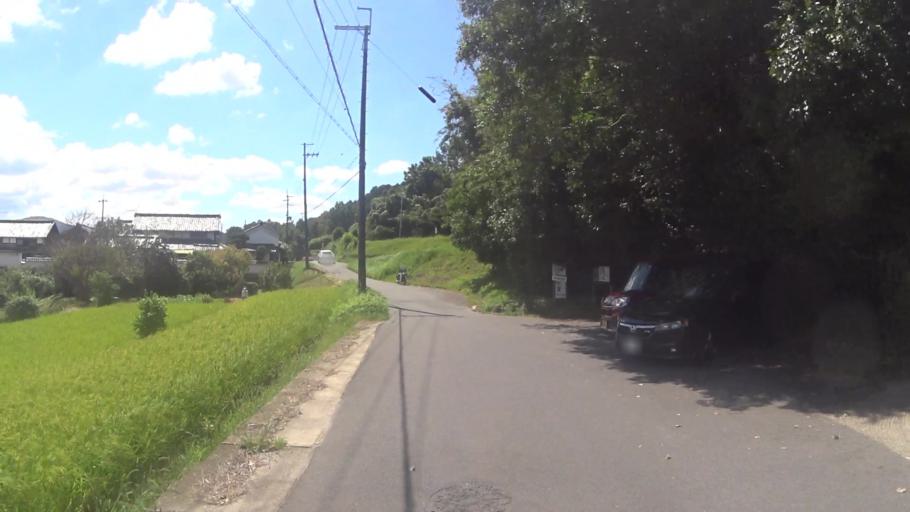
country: JP
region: Nara
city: Nara-shi
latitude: 34.7411
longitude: 135.8545
